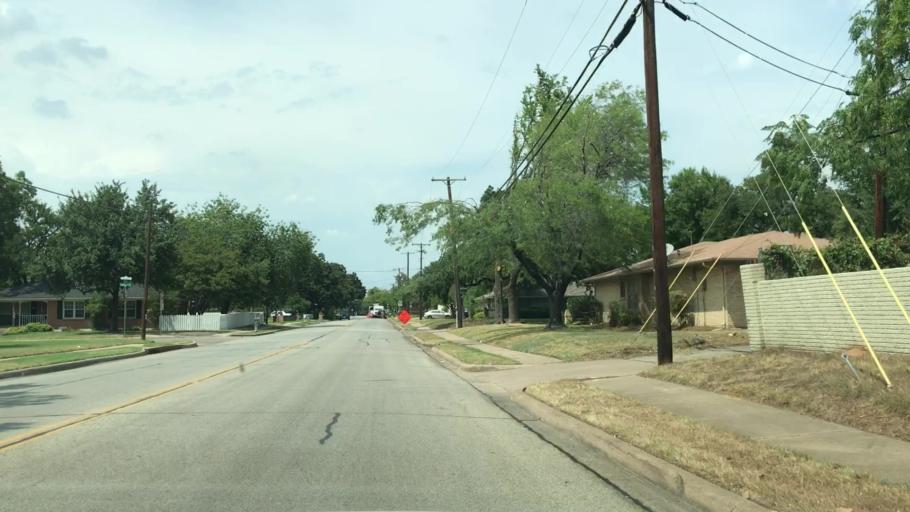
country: US
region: Texas
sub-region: Dallas County
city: Irving
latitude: 32.8402
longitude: -96.9427
